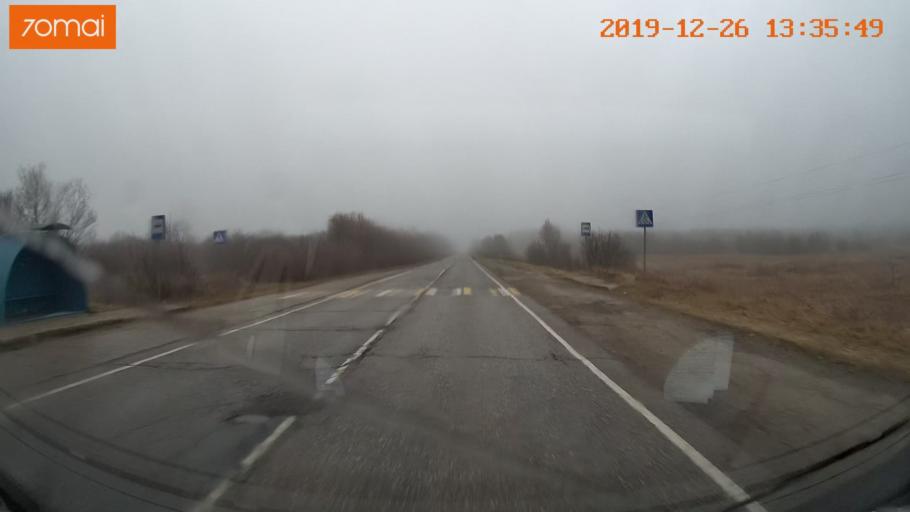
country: RU
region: Vologda
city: Sheksna
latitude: 58.7888
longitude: 38.3463
